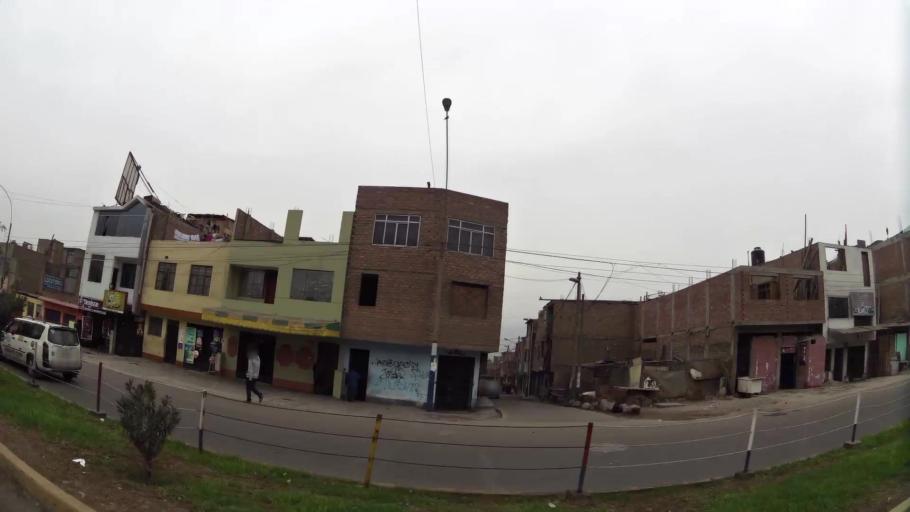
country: PE
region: Lima
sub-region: Lima
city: Independencia
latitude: -11.9675
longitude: -77.0102
